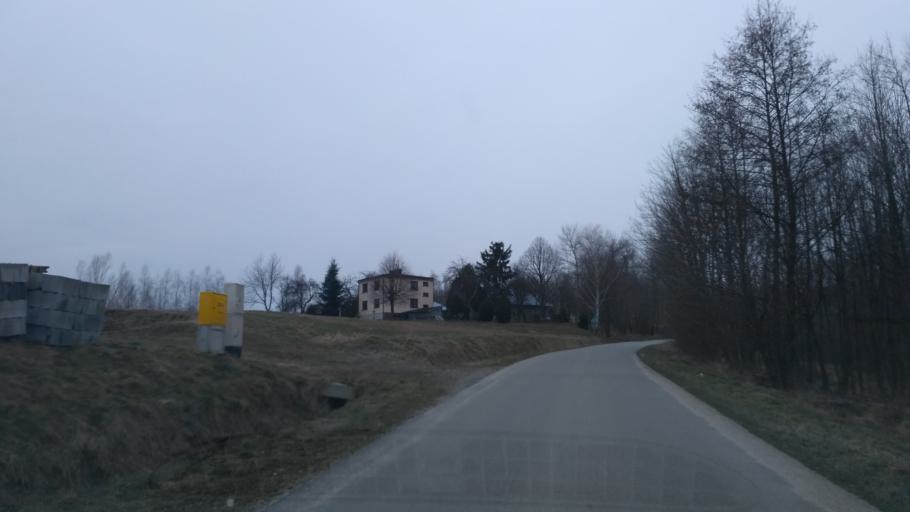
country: PL
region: Subcarpathian Voivodeship
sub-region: Powiat rzeszowski
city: Chmielnik
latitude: 49.9766
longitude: 22.1457
